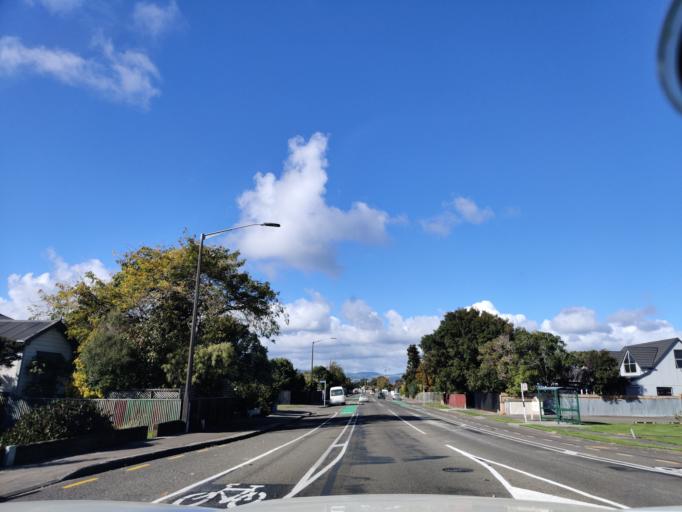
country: NZ
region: Manawatu-Wanganui
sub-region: Palmerston North City
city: Palmerston North
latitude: -40.3496
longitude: 175.5971
